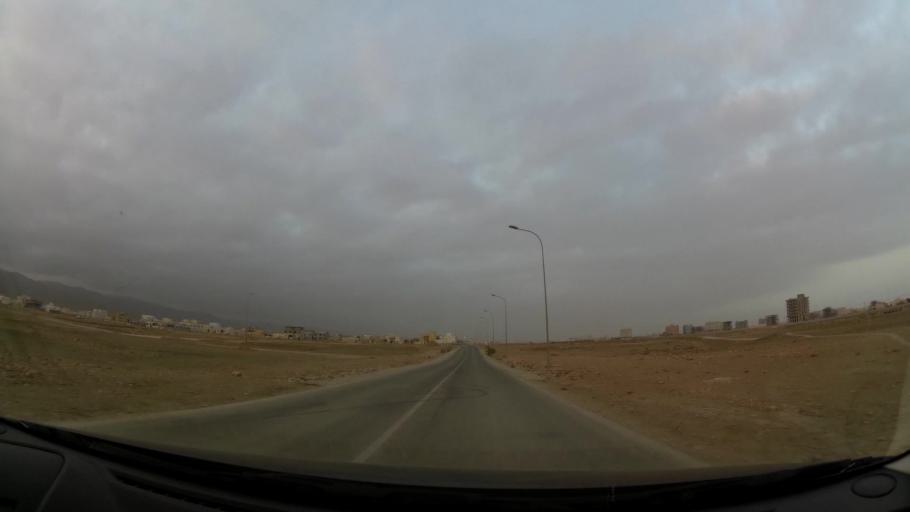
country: OM
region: Zufar
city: Salalah
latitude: 17.0265
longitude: 54.0183
